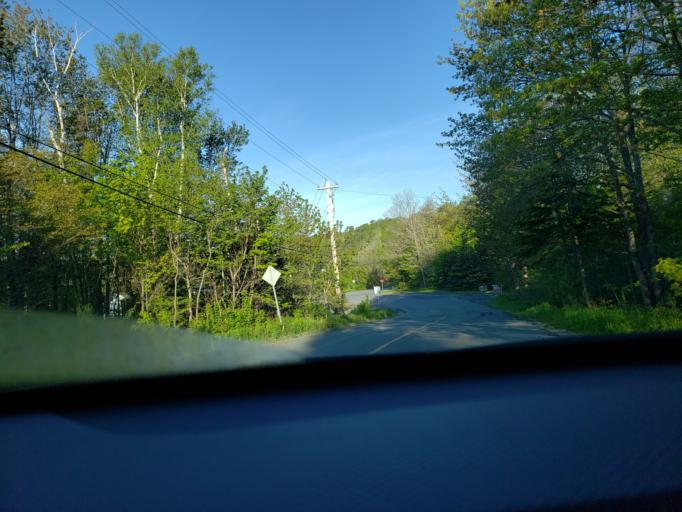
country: CA
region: Nova Scotia
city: Cole Harbour
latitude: 44.7397
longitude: -63.3812
